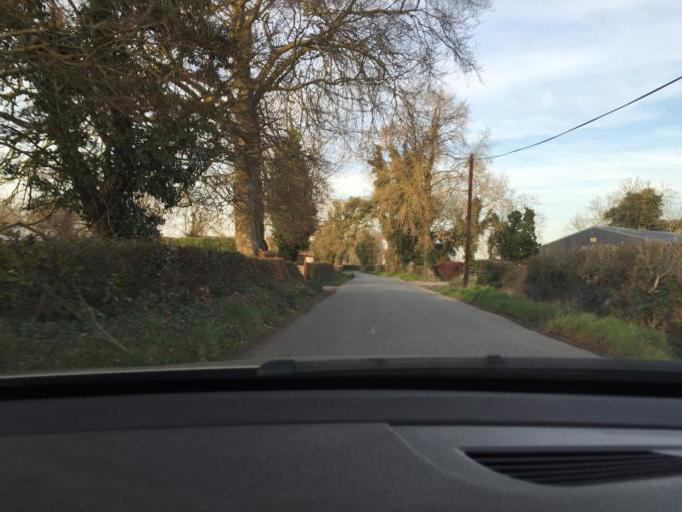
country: IE
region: Leinster
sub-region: An Mhi
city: Dunboyne
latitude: 53.4405
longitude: -6.4468
